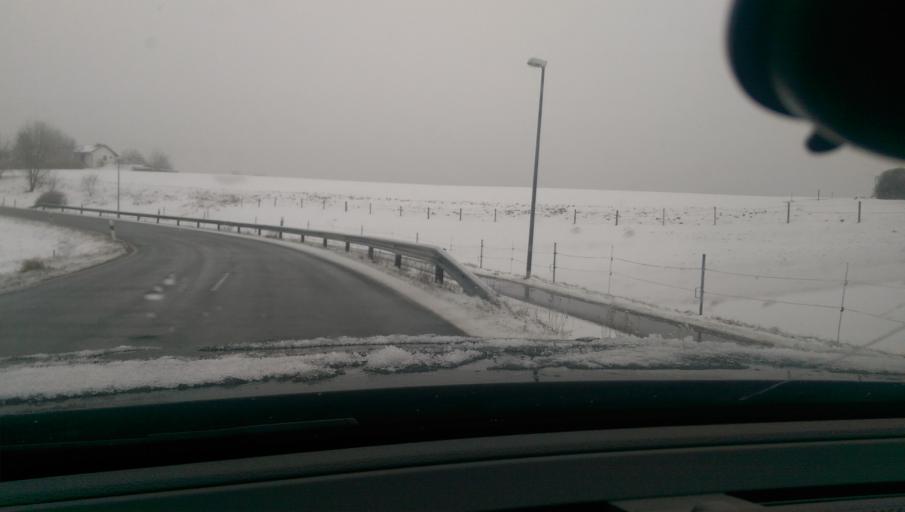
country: DE
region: Bavaria
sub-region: Lower Bavaria
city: Haselbach
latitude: 48.6564
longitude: 13.4009
